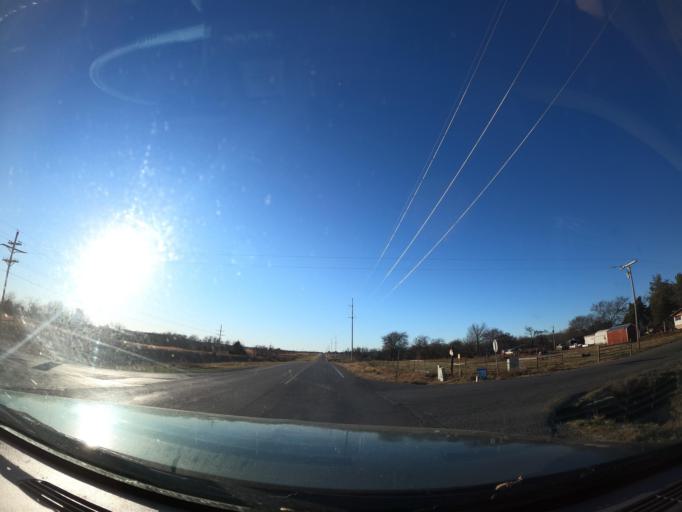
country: US
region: Oklahoma
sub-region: Latimer County
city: Wilburton
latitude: 34.9130
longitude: -95.4020
